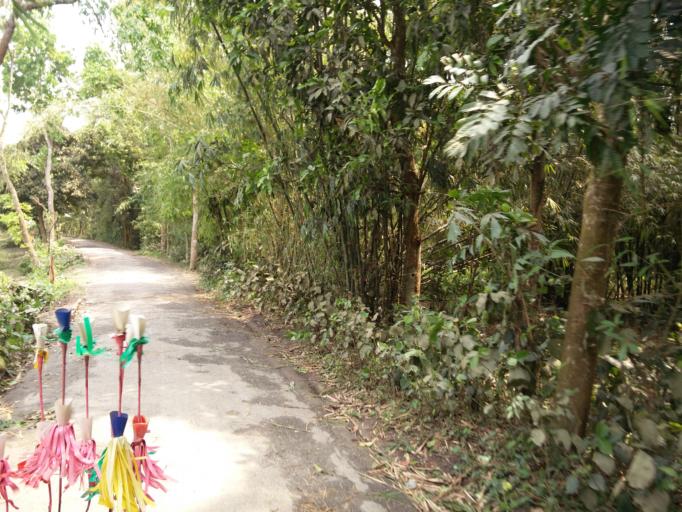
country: BD
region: Dhaka
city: Sherpur
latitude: 24.9336
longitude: 90.1610
